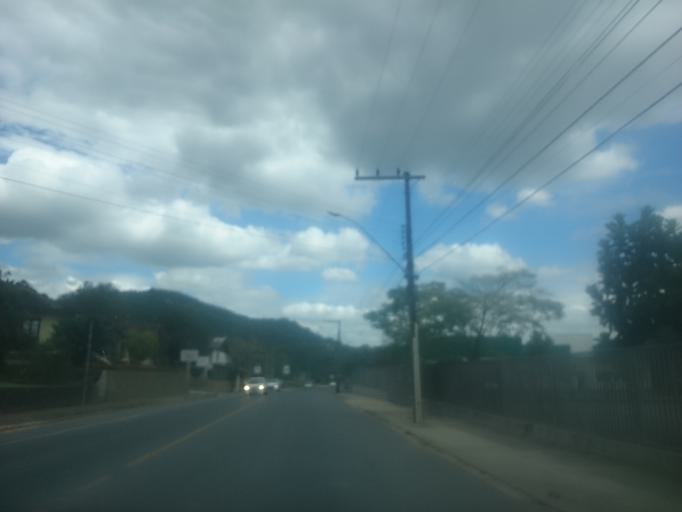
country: BR
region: Santa Catarina
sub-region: Pomerode
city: Pomerode
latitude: -26.7192
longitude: -49.1676
